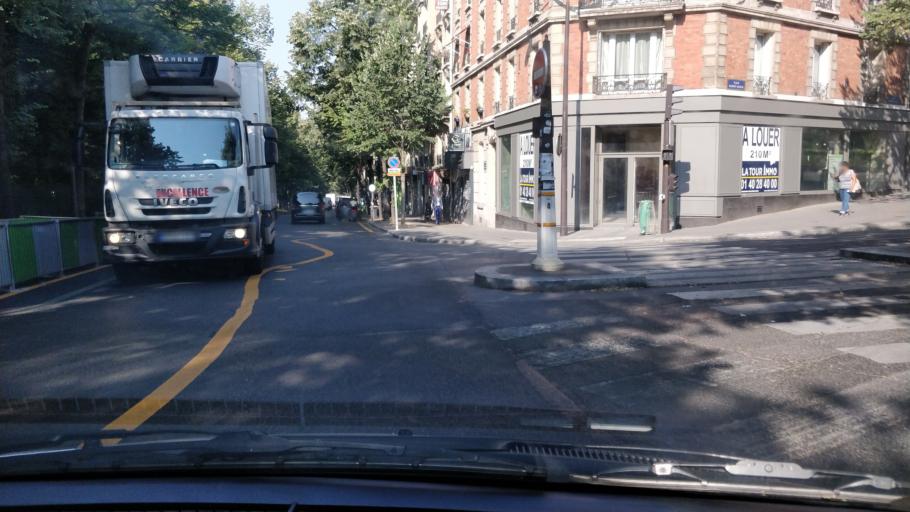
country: FR
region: Ile-de-France
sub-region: Departement de Seine-Saint-Denis
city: Bagnolet
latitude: 48.8648
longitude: 2.3947
